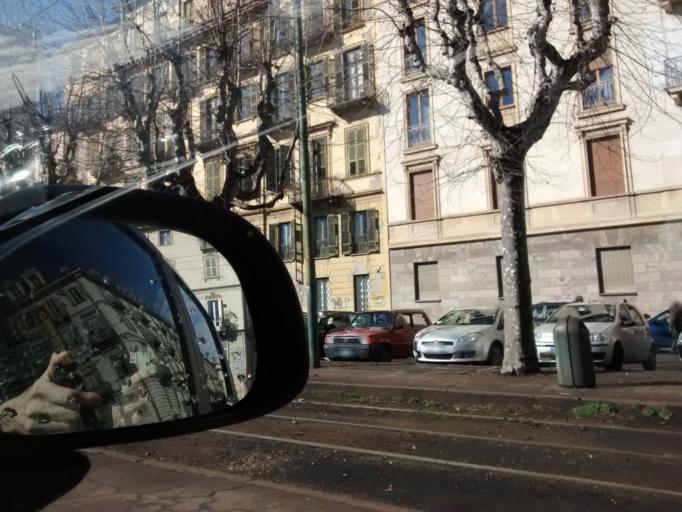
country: IT
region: Piedmont
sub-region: Provincia di Torino
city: Turin
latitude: 45.0626
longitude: 7.6940
